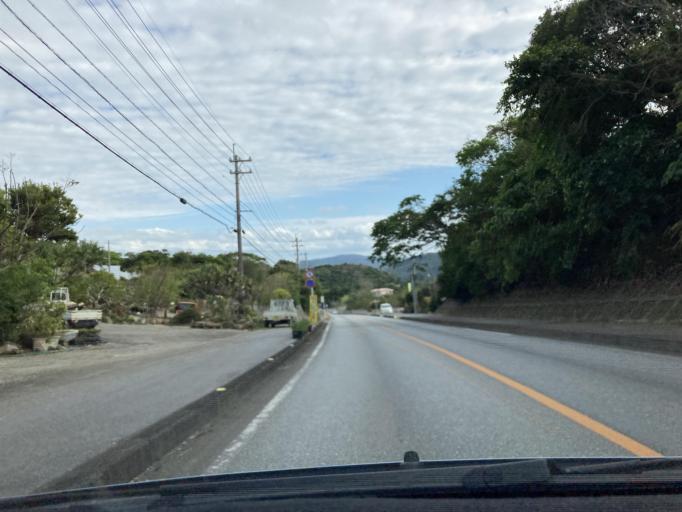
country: JP
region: Okinawa
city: Nago
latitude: 26.6606
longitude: 127.9811
